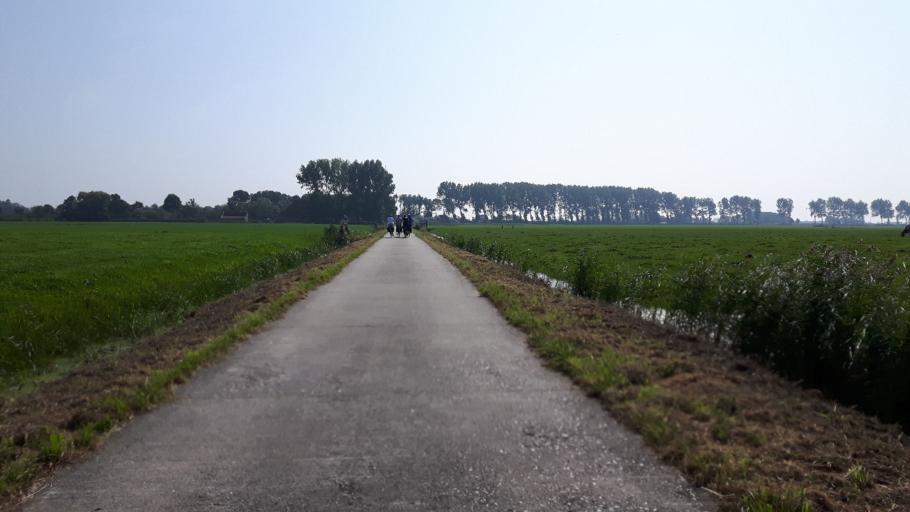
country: NL
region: Friesland
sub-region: Sudwest Fryslan
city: Workum
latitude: 52.9509
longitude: 5.4220
